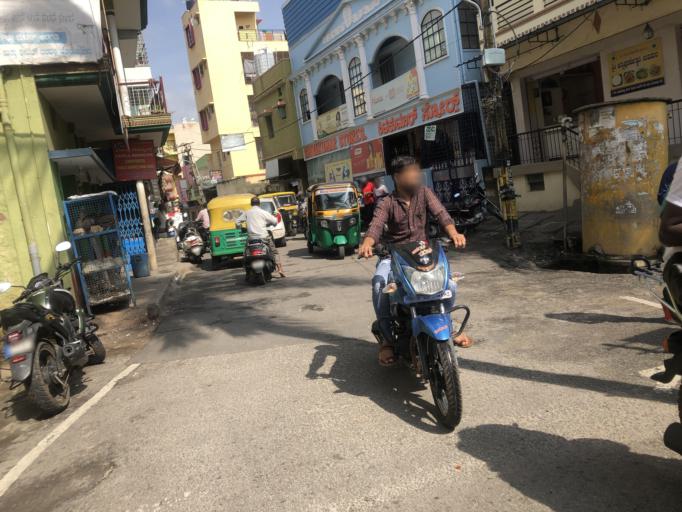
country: IN
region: Karnataka
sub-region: Bangalore Urban
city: Bangalore
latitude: 12.9296
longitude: 77.5382
